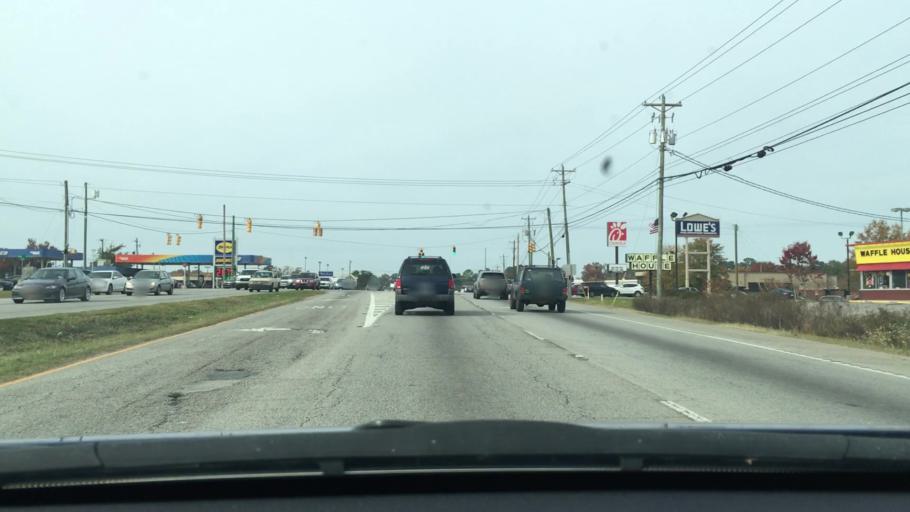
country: US
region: South Carolina
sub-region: Richland County
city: Forest Acres
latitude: 33.9651
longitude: -80.9432
